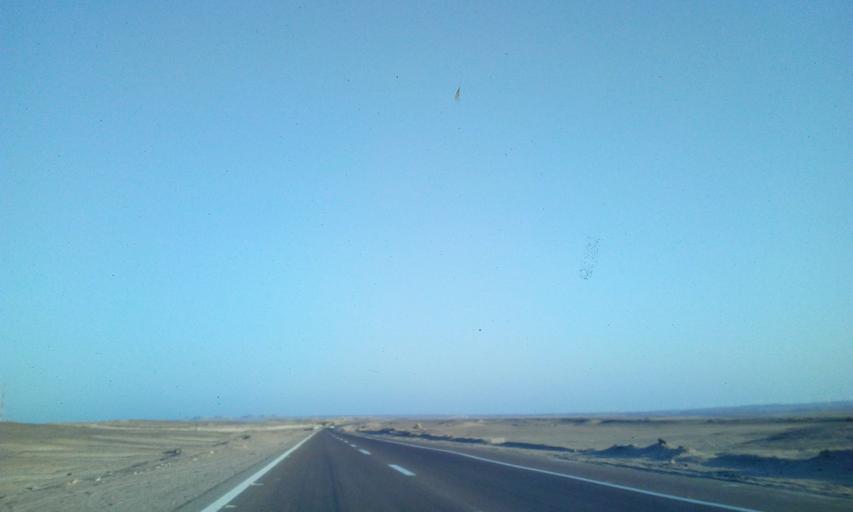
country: EG
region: South Sinai
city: Tor
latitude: 28.1727
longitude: 33.2205
